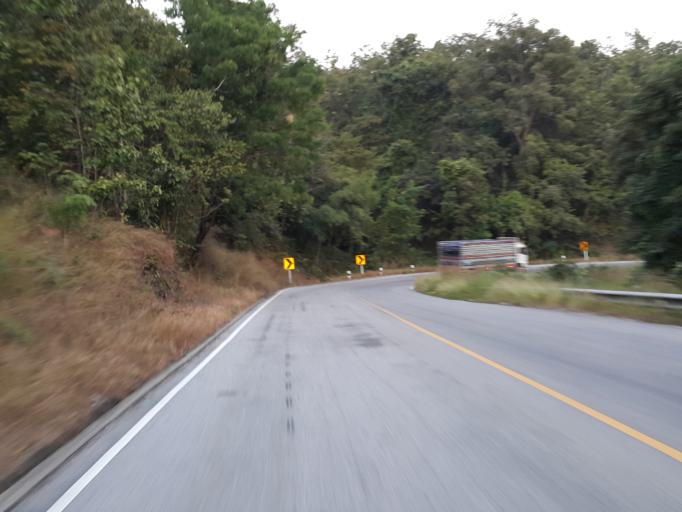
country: TH
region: Lampang
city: Thoen
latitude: 17.6521
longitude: 99.1220
